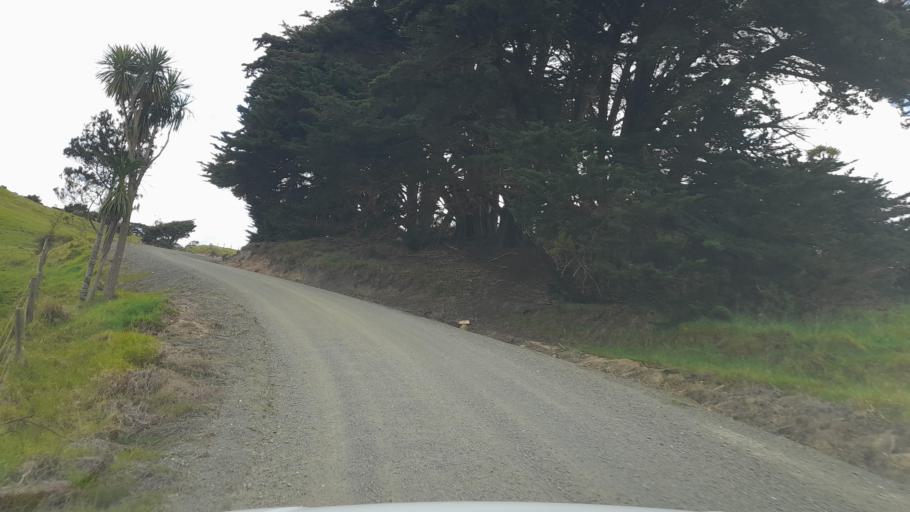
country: NZ
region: Auckland
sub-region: Auckland
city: Wellsford
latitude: -36.2047
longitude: 174.3371
